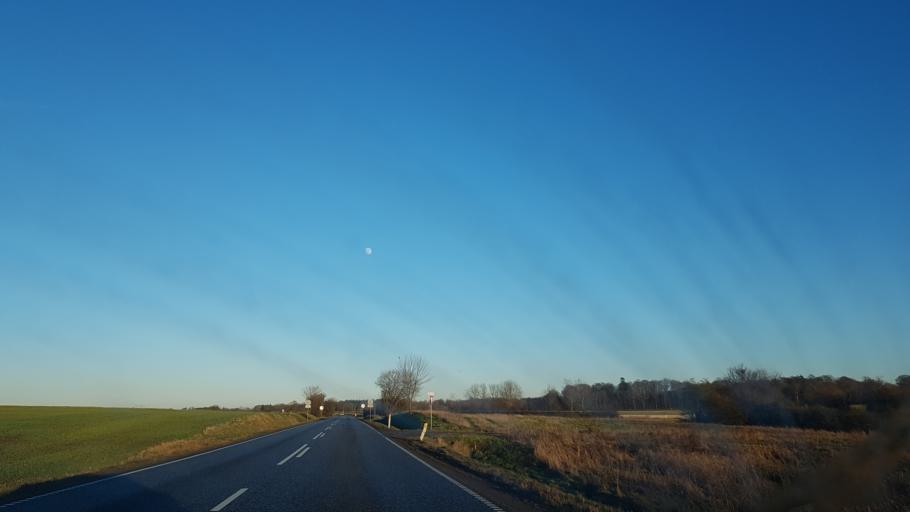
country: DK
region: South Denmark
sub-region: Kolding Kommune
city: Kolding
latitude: 55.4339
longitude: 9.4648
